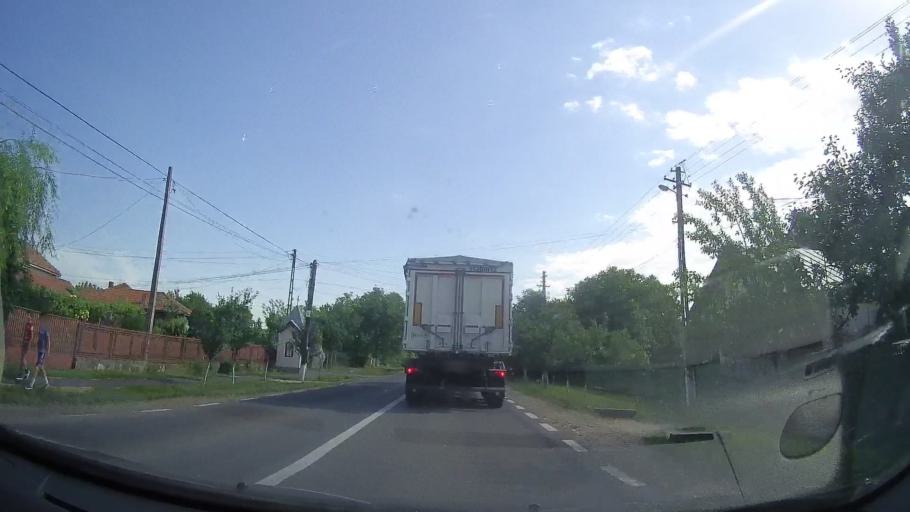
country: RO
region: Prahova
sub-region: Comuna Izvoarele
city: Homoraciu
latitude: 45.2520
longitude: 26.0249
